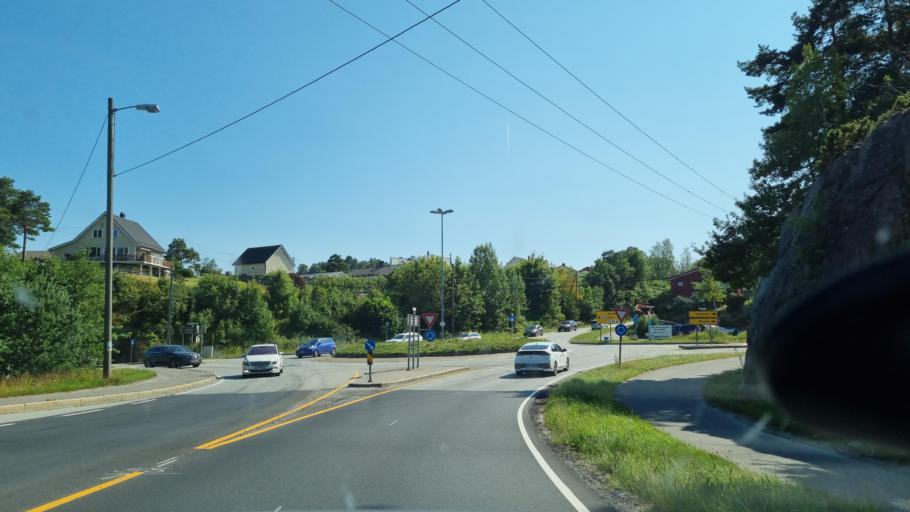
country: NO
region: Aust-Agder
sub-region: Arendal
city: Arendal
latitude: 58.4674
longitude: 8.8249
